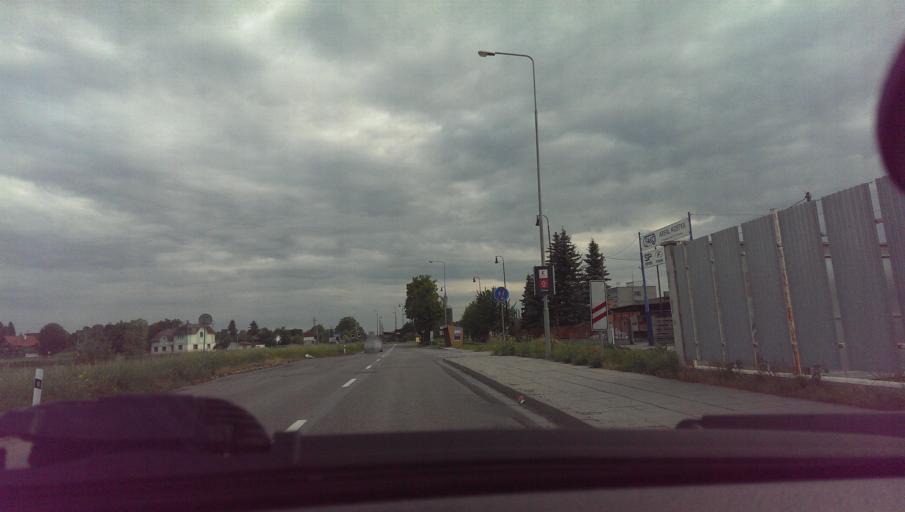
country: CZ
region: Zlin
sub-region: Okres Kromeriz
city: Kromeriz
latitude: 49.2820
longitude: 17.4026
